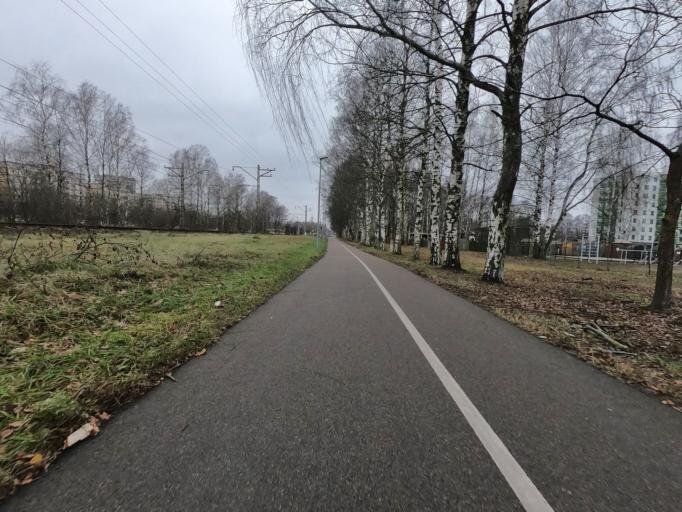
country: LV
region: Marupe
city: Marupe
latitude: 56.9504
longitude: 24.0061
